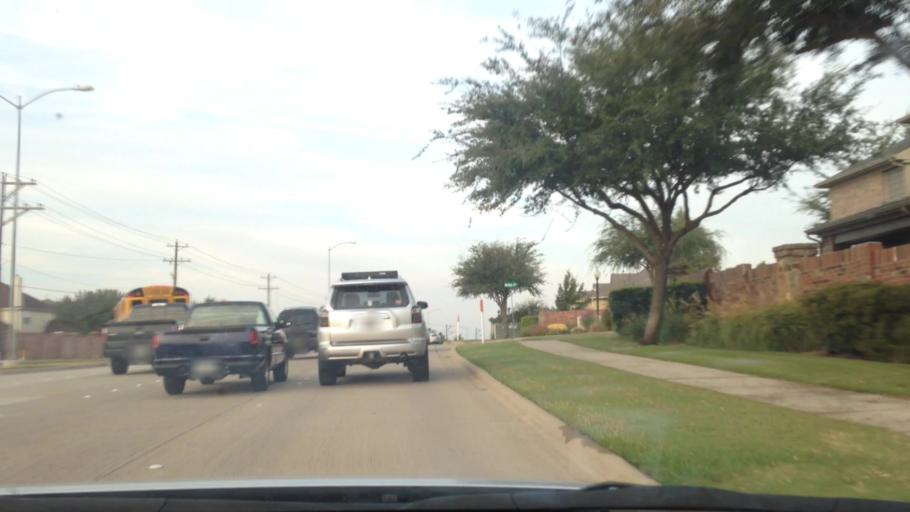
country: US
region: Texas
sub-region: Collin County
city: Frisco
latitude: 33.1073
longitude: -96.7625
